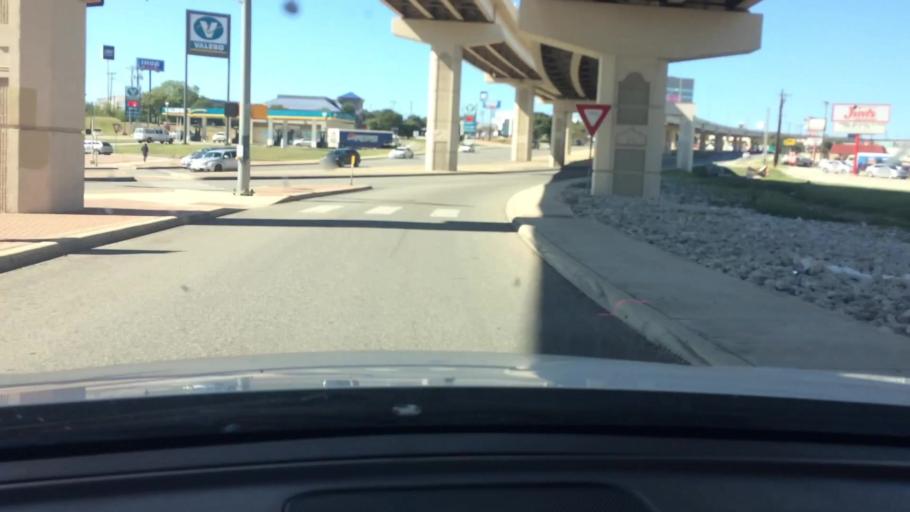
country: US
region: Texas
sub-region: Bexar County
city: Leon Valley
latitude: 29.4831
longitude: -98.6005
